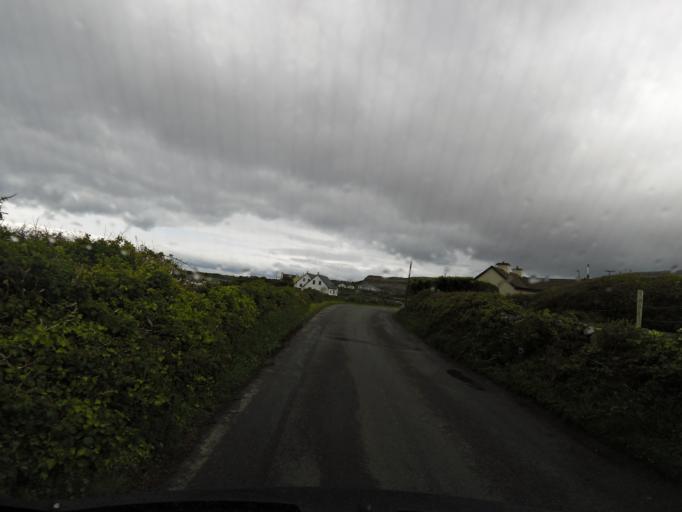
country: IE
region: Connaught
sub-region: County Galway
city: Bearna
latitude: 53.1310
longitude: -9.2754
